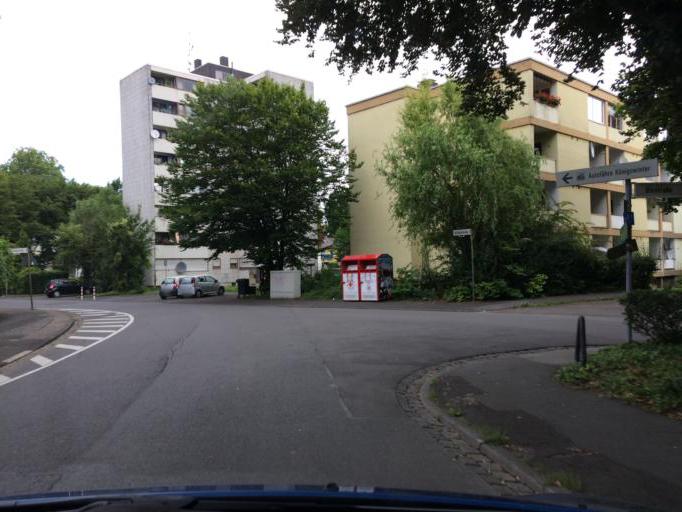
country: DE
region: North Rhine-Westphalia
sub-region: Regierungsbezirk Koln
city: Konigswinter
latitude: 50.6679
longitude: 7.1871
